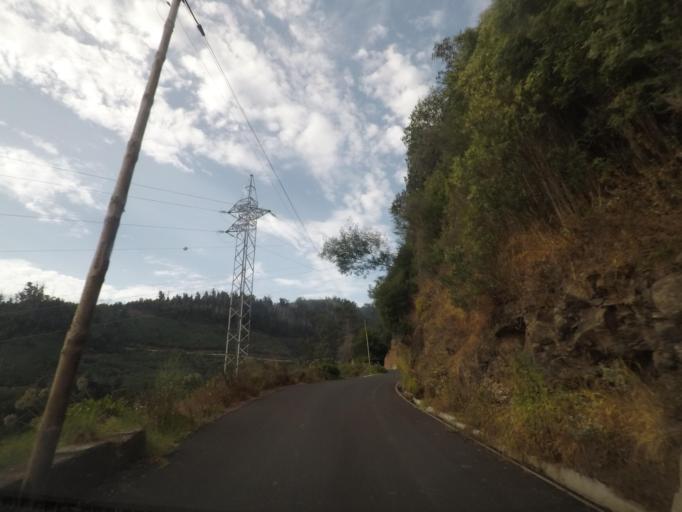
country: PT
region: Madeira
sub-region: Calheta
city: Arco da Calheta
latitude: 32.7393
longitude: -17.1536
